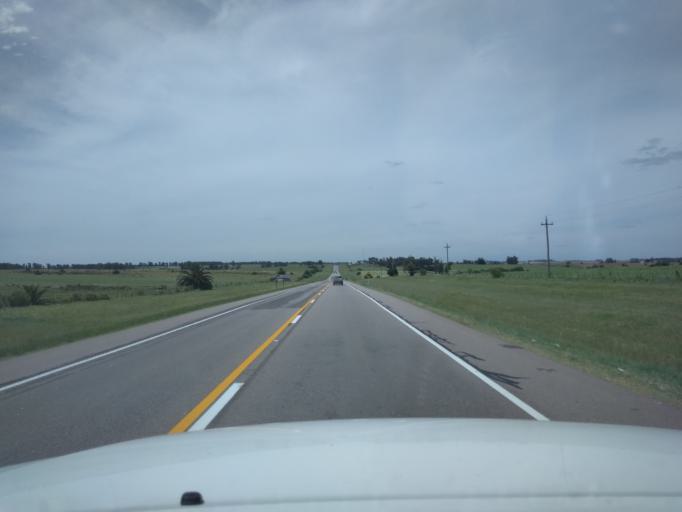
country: UY
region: Florida
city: Florida
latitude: -34.2254
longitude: -56.2107
